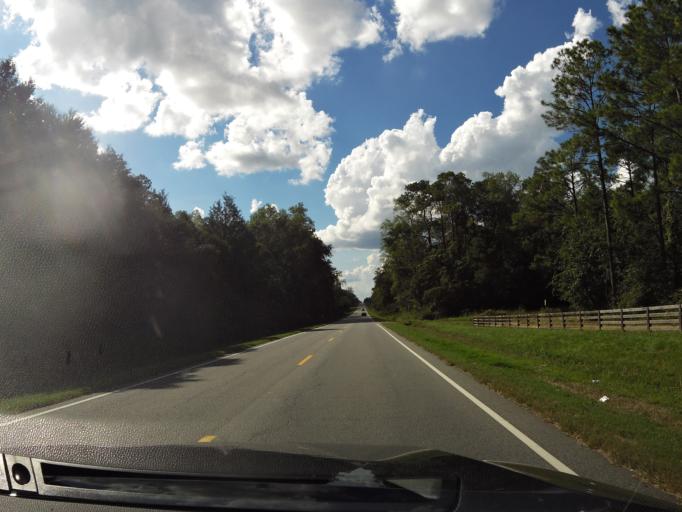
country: US
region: Georgia
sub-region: Lowndes County
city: Valdosta
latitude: 30.8086
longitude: -83.2199
